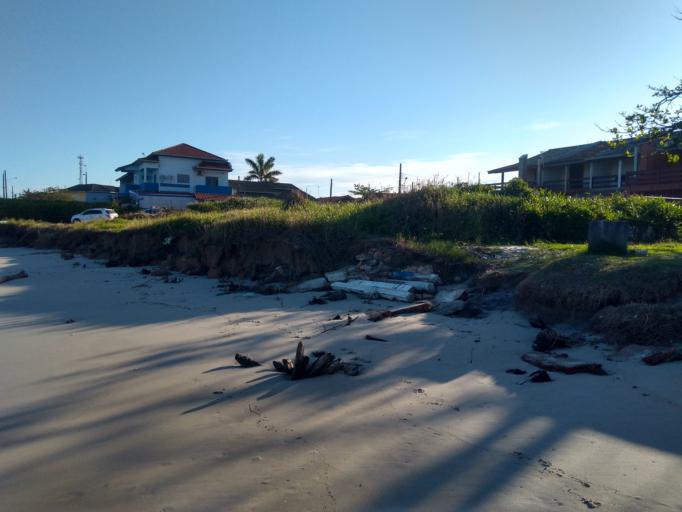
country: BR
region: Parana
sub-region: Guaratuba
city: Guaratuba
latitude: -26.0585
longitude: -48.6110
